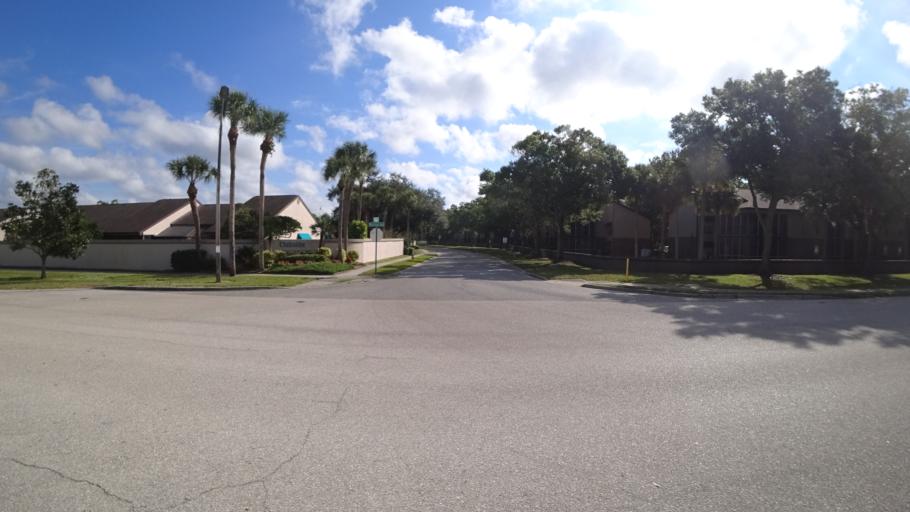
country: US
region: Florida
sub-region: Sarasota County
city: Desoto Lakes
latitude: 27.3929
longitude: -82.4871
